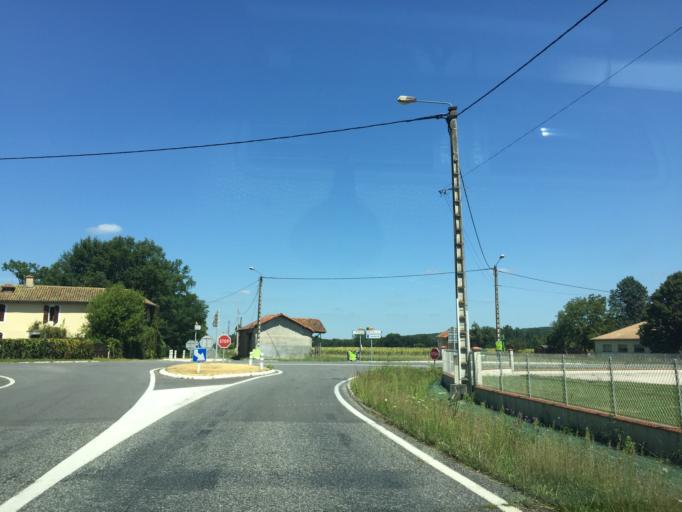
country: FR
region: Midi-Pyrenees
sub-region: Departement des Hautes-Pyrenees
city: Trie-sur-Baise
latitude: 43.2992
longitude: 0.4537
